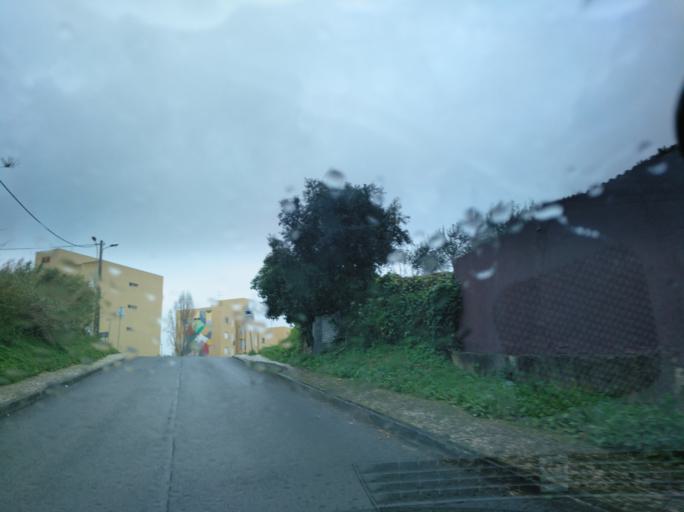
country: PT
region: Lisbon
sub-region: Odivelas
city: Pontinha
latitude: 38.7701
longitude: -9.1953
